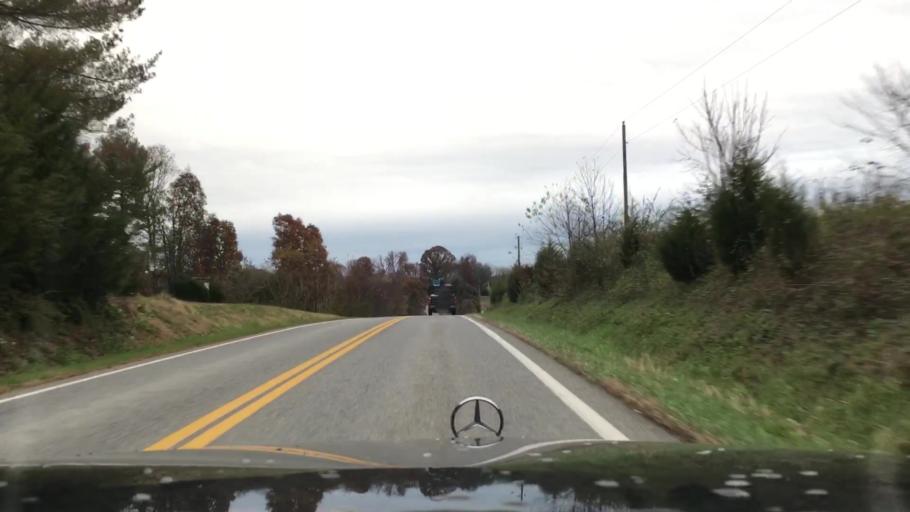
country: US
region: Virginia
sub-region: Campbell County
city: Altavista
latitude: 37.2151
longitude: -79.2967
